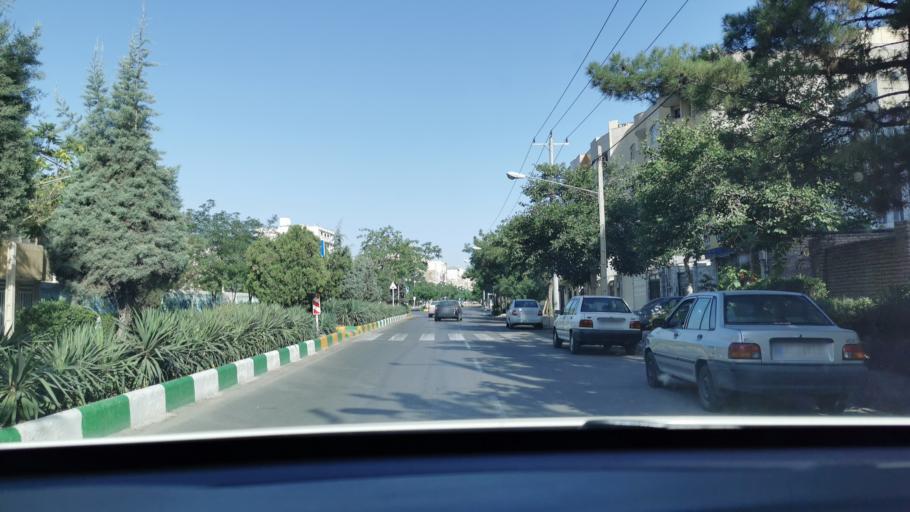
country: IR
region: Razavi Khorasan
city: Mashhad
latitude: 36.3381
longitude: 59.5099
